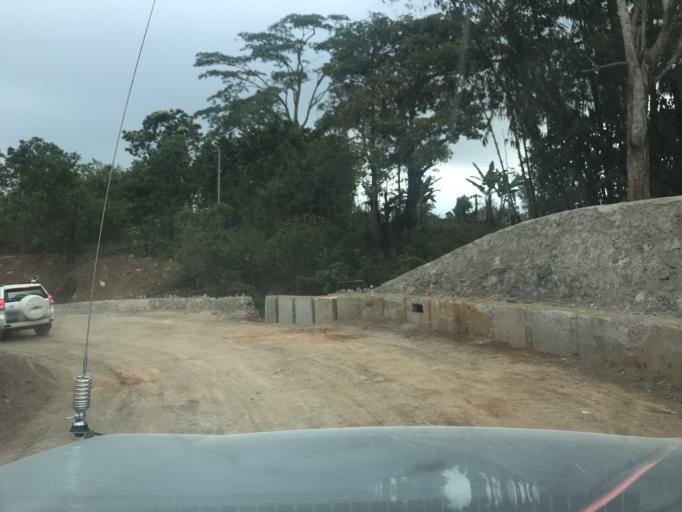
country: TL
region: Ainaro
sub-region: Ainaro
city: Ainaro
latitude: -8.9945
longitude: 125.5069
